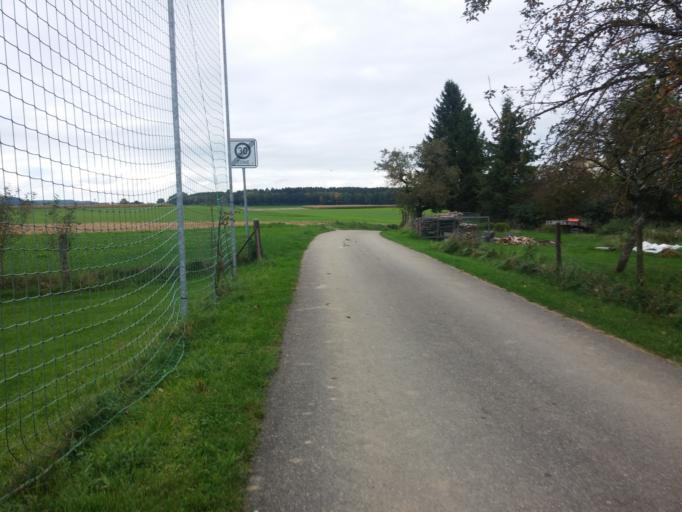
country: DE
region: Baden-Wuerttemberg
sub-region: Tuebingen Region
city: Tannheim
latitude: 47.9732
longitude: 10.0877
